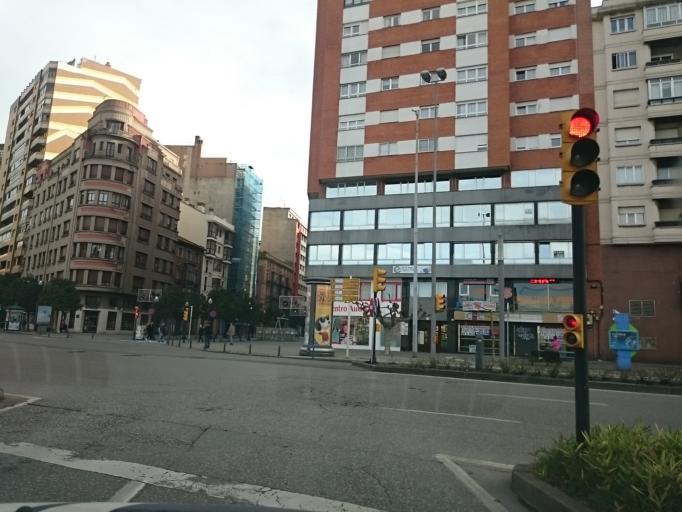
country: ES
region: Asturias
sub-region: Province of Asturias
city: Gijon
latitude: 43.5415
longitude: -5.6443
